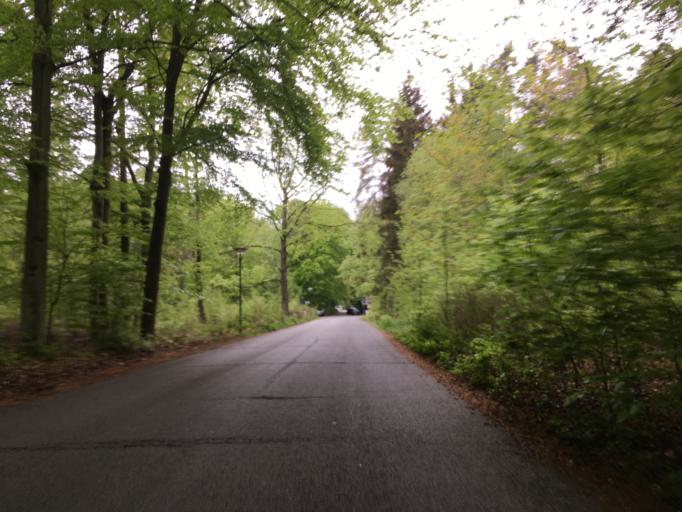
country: DE
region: Brandenburg
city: Wandlitz
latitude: 52.7275
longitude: 13.4978
